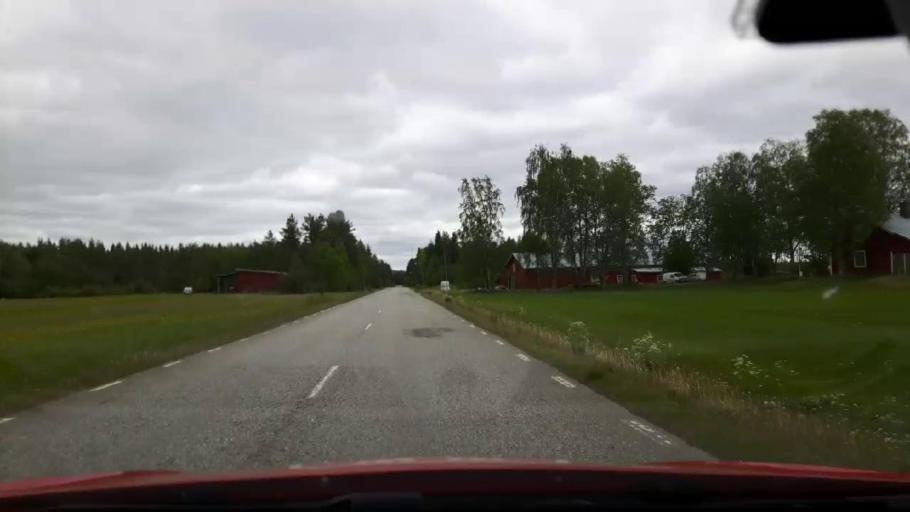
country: SE
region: Jaemtland
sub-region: Ragunda Kommun
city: Hammarstrand
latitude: 63.2269
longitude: 15.9291
